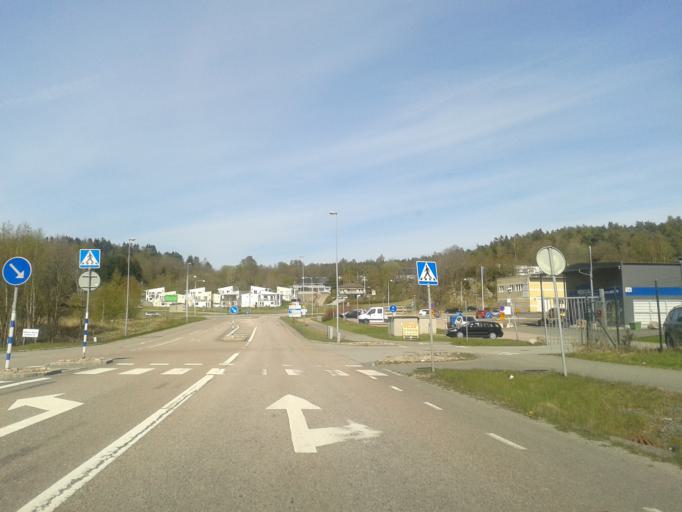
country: SE
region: Vaestra Goetaland
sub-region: Kungalvs Kommun
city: Kungalv
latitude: 57.8877
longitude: 11.9481
